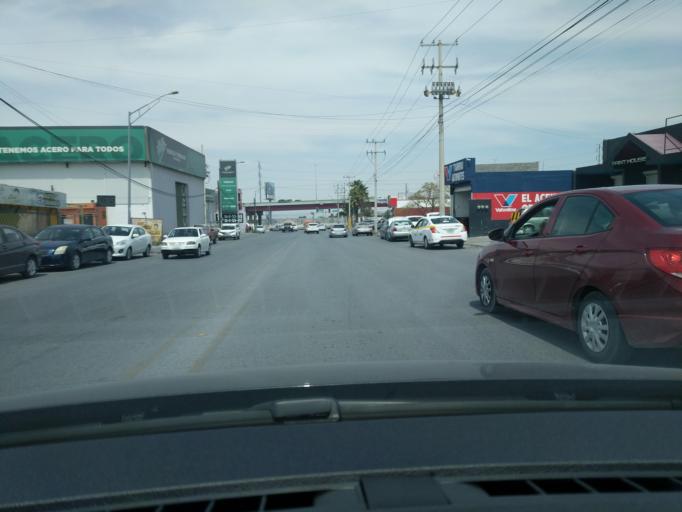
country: MX
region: Coahuila
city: Saltillo
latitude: 25.4290
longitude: -100.9468
